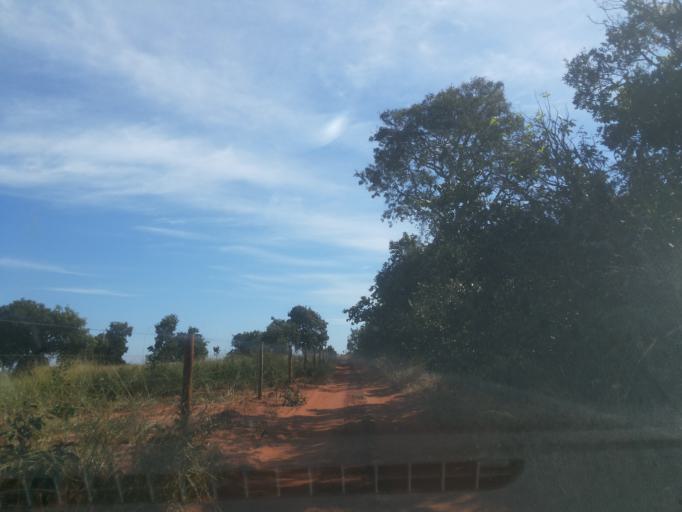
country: BR
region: Minas Gerais
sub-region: Ituiutaba
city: Ituiutaba
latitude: -19.1205
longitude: -49.3826
